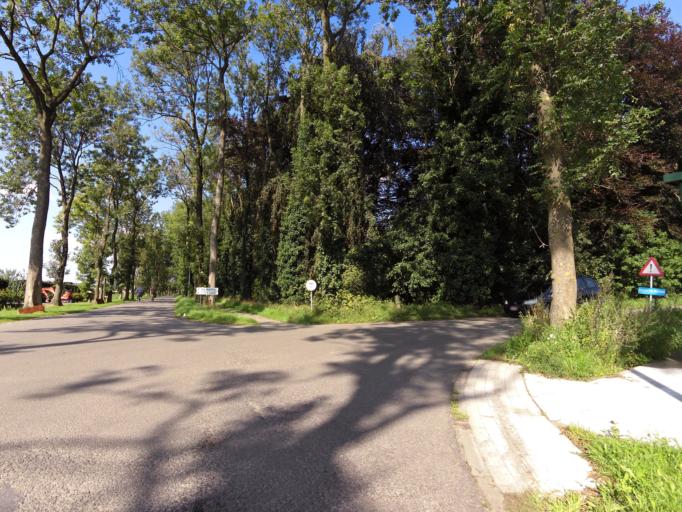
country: BE
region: Flanders
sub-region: Provincie West-Vlaanderen
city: Zedelgem
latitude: 51.1993
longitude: 3.1503
